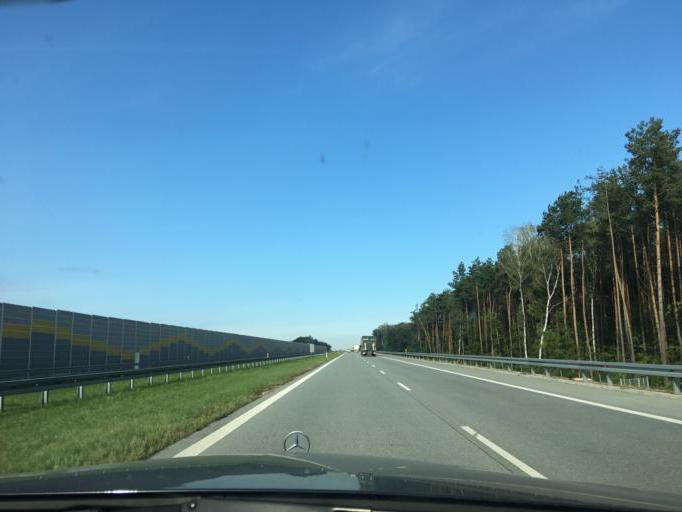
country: PL
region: Lodz Voivodeship
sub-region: Powiat zdunskowolski
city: Zdunska Wola
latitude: 51.5697
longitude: 18.9686
